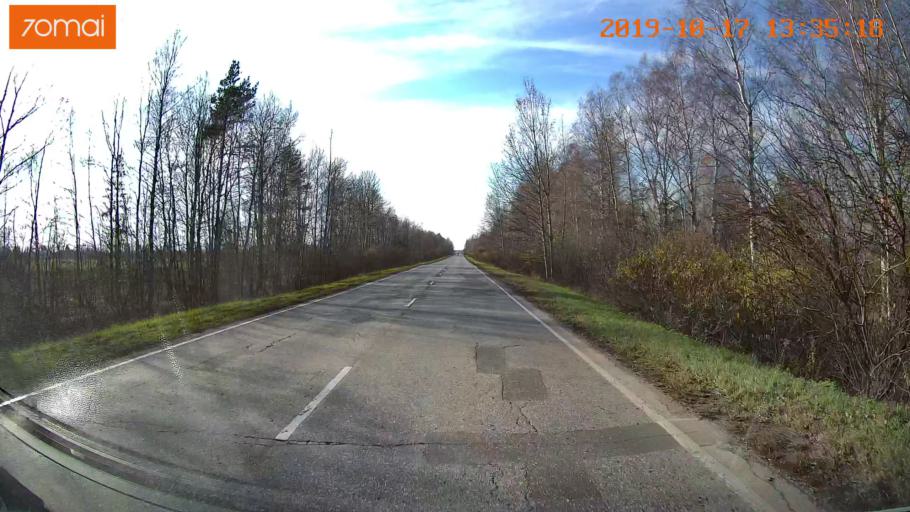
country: RU
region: Vladimir
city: Velikodvorskiy
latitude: 55.1427
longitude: 40.6931
